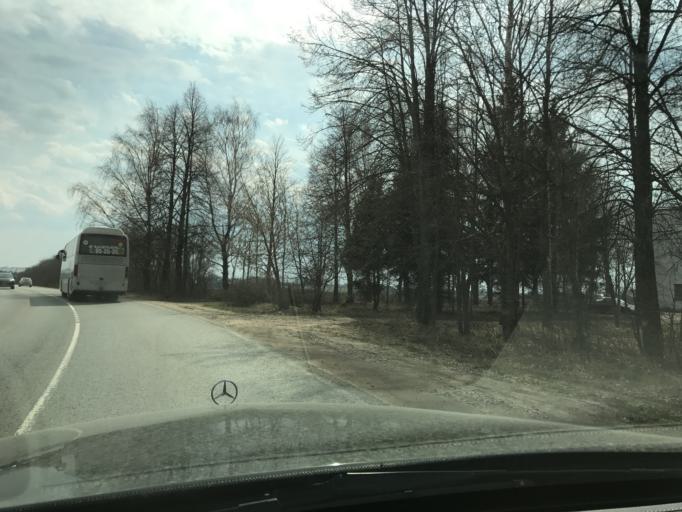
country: RU
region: Vladimir
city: Suzdal'
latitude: 56.4202
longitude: 40.4281
